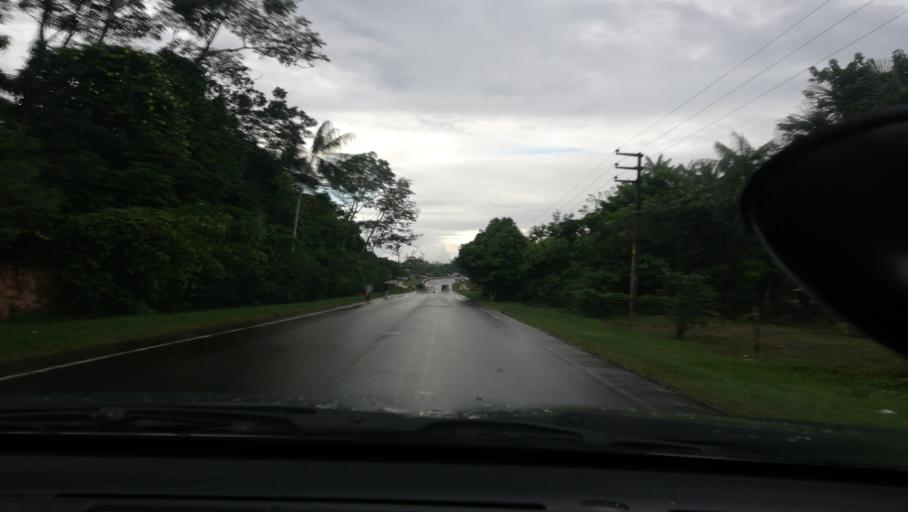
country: PE
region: Loreto
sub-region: Provincia de Maynas
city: Iquitos
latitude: -3.8929
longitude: -73.3495
